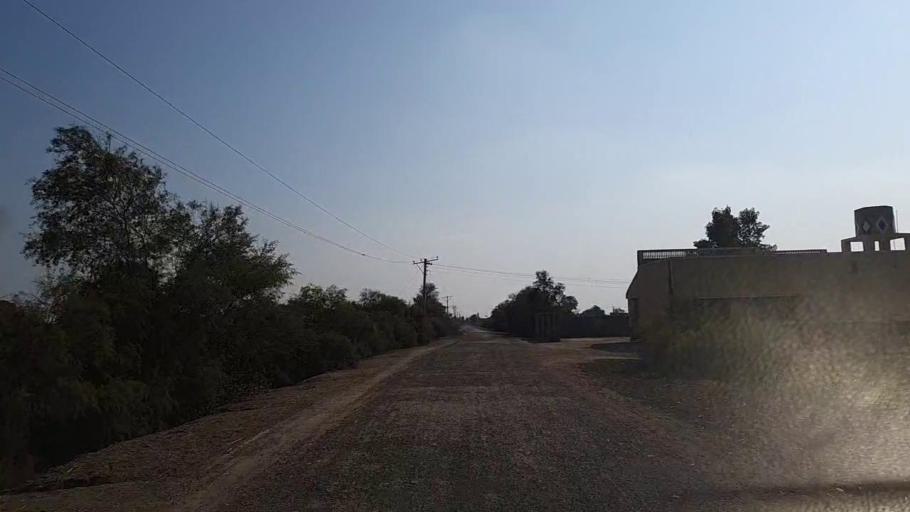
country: PK
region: Sindh
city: Jam Sahib
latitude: 26.2816
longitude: 68.6046
